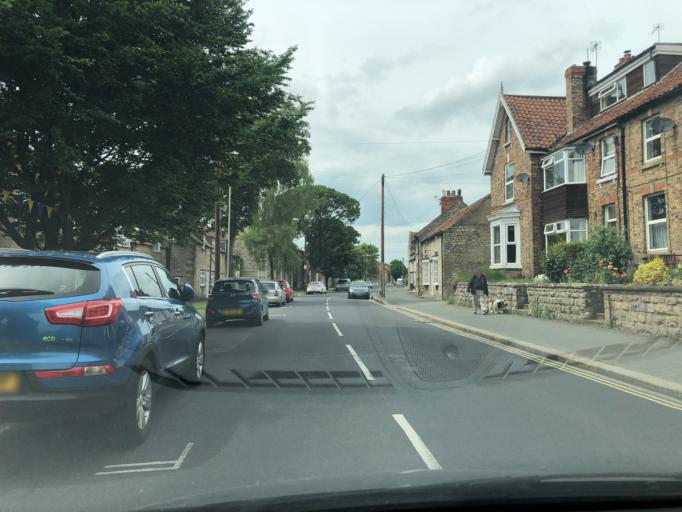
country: GB
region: England
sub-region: North Yorkshire
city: Pickering
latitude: 54.2462
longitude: -0.7860
